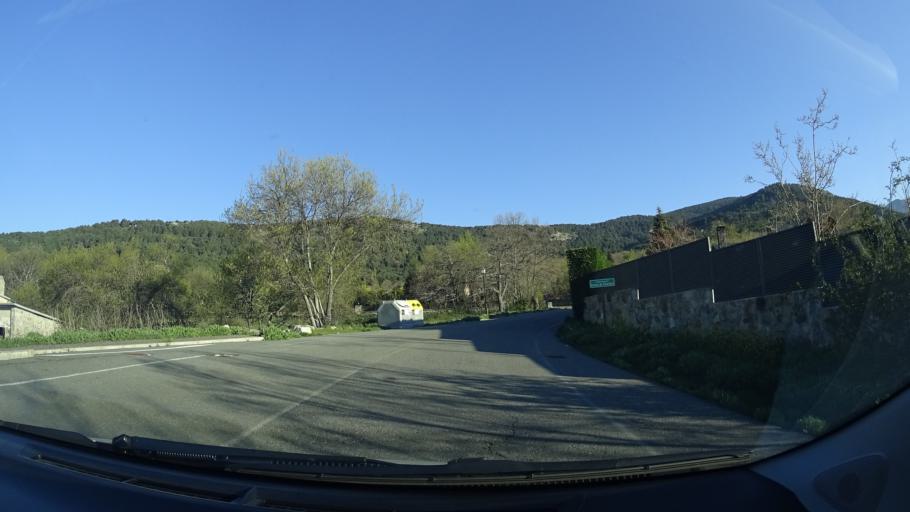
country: ES
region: Madrid
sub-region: Provincia de Madrid
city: Navacerrada
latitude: 40.7366
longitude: -4.0067
